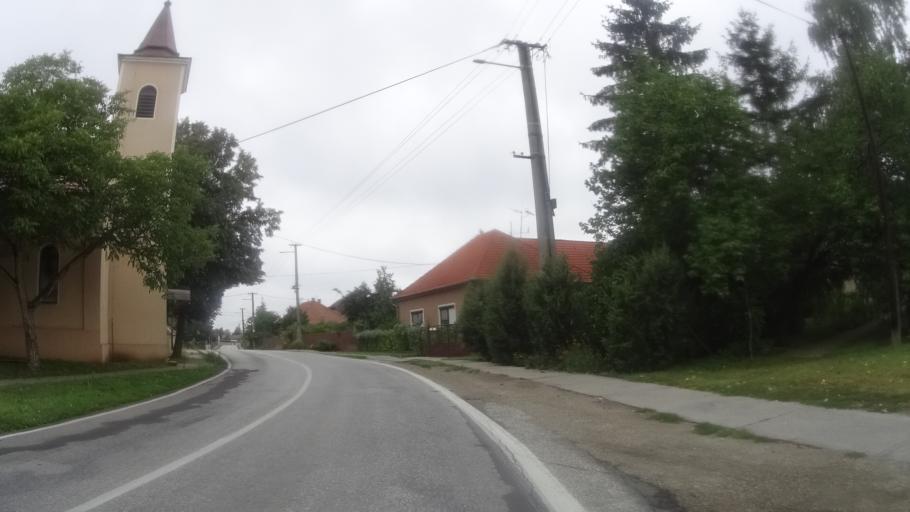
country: HU
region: Komarom-Esztergom
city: Neszmely
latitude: 47.7468
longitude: 18.3707
